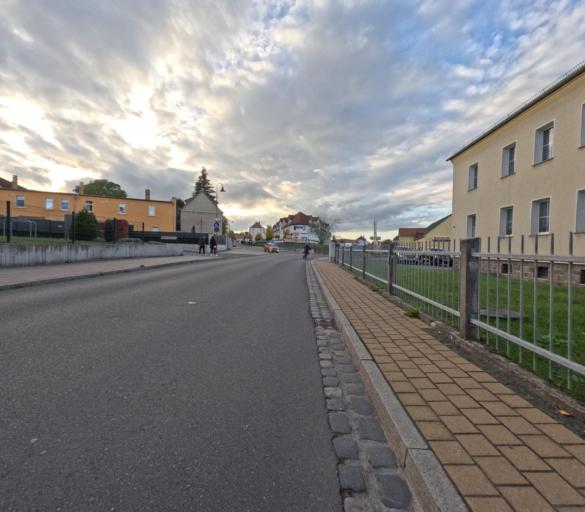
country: DE
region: Saxony
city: Grimma
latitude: 51.2359
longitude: 12.7183
